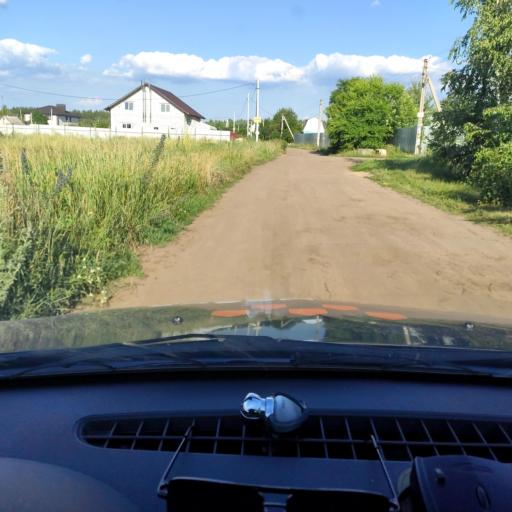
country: RU
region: Voronezj
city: Podgornoye
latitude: 51.8647
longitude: 39.1756
